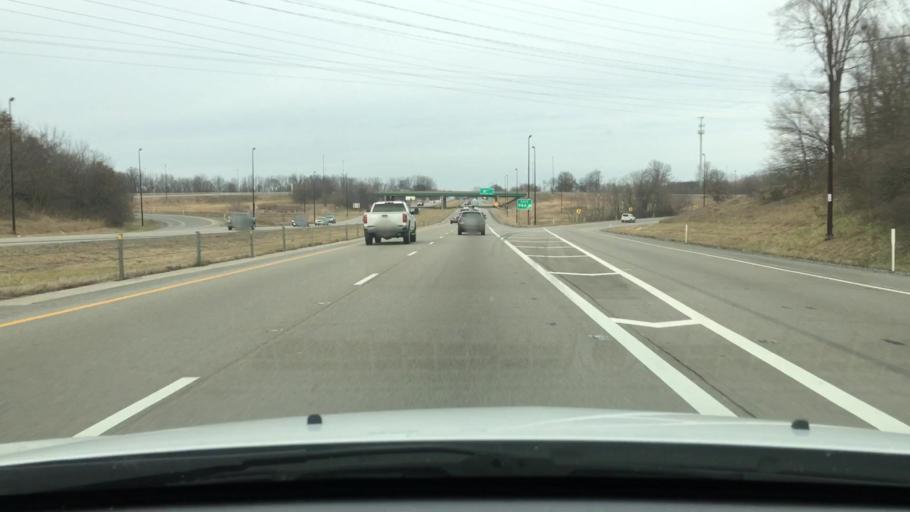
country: US
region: Illinois
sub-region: Sangamon County
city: Grandview
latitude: 39.7981
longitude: -89.5961
